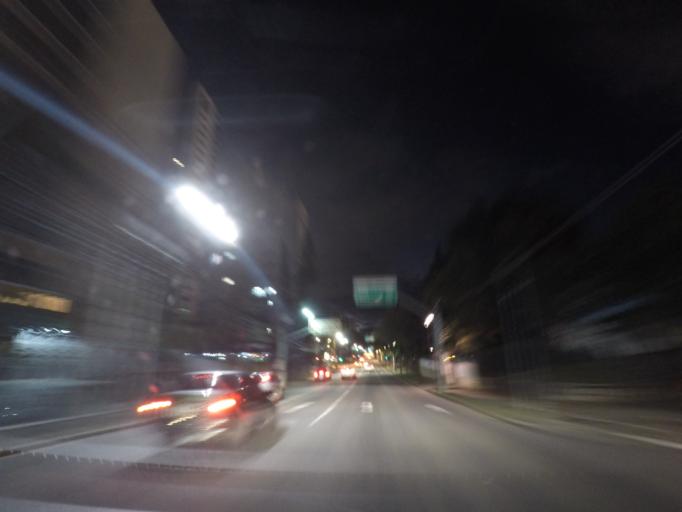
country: BR
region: Parana
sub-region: Curitiba
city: Curitiba
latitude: -25.4178
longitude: -49.2672
